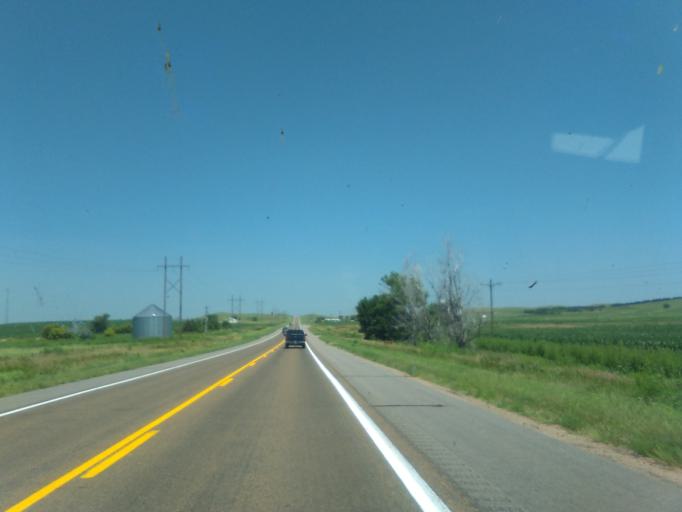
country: US
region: Nebraska
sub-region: Lincoln County
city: North Platte
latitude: 40.8136
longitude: -100.7537
